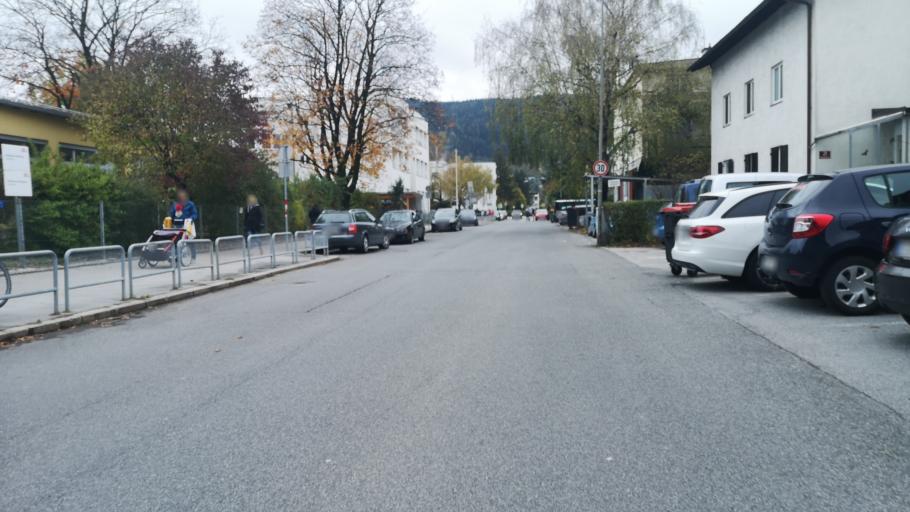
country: AT
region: Tyrol
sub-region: Innsbruck Stadt
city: Innsbruck
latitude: 47.2608
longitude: 11.3682
